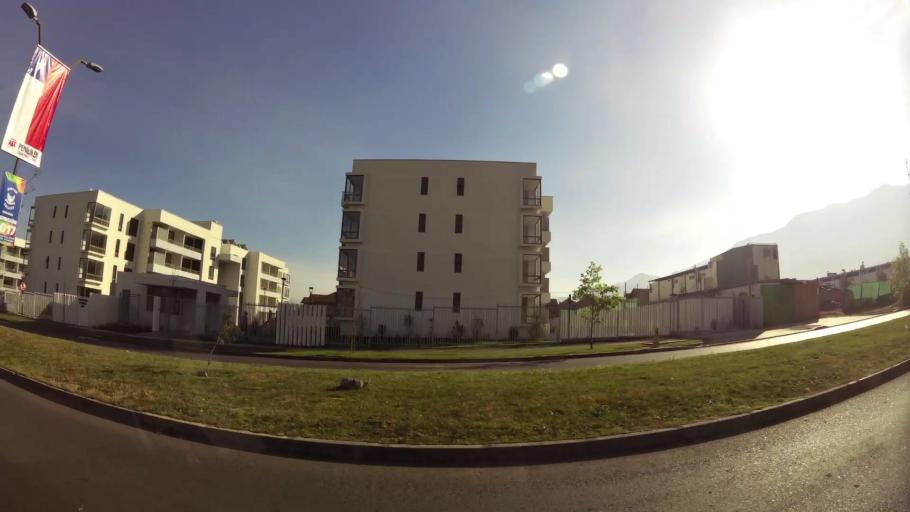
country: CL
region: Santiago Metropolitan
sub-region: Provincia de Santiago
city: Villa Presidente Frei, Nunoa, Santiago, Chile
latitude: -33.4886
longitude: -70.5511
